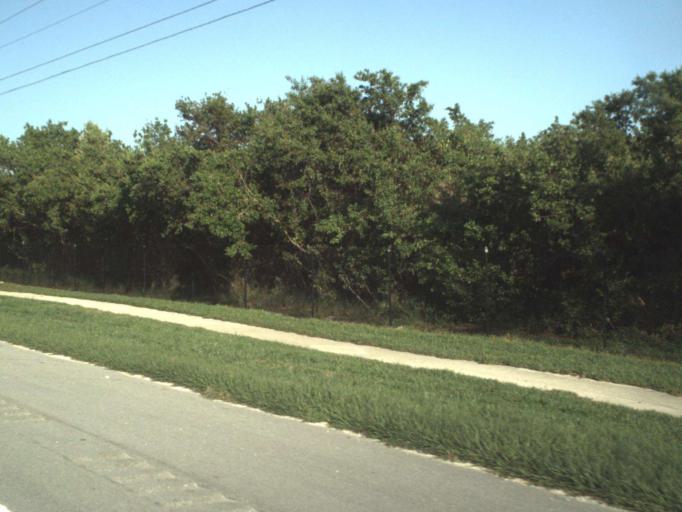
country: US
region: Florida
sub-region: Monroe County
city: Islamorada
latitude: 24.8085
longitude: -80.8351
